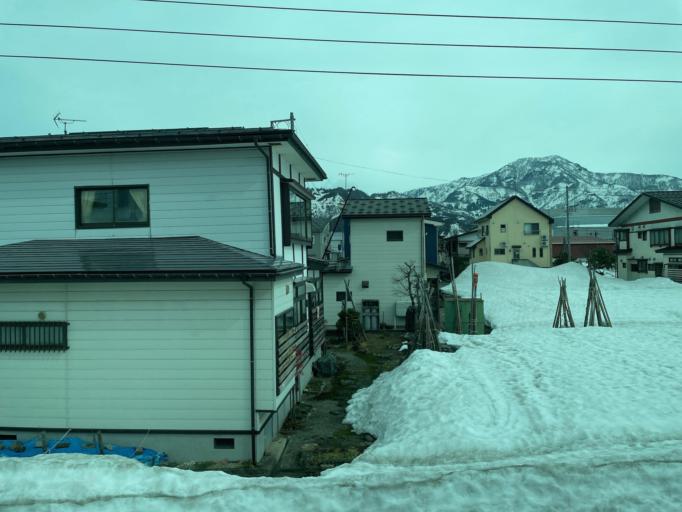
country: JP
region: Niigata
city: Muikamachi
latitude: 37.0625
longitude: 138.8729
